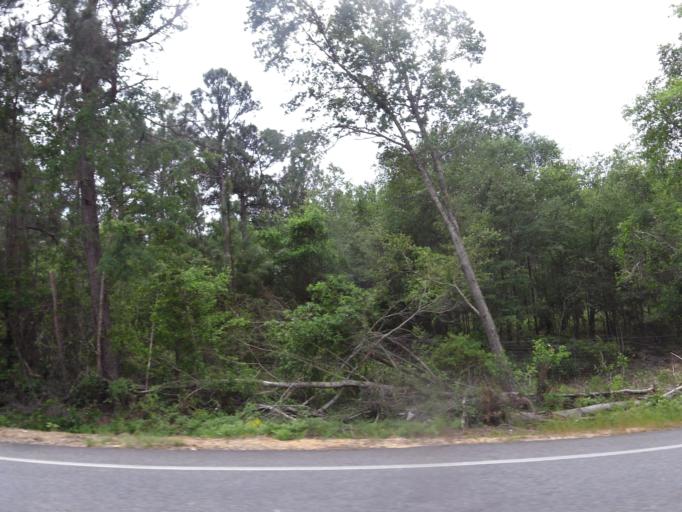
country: US
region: Georgia
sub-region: Candler County
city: Metter
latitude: 32.3888
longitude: -82.1754
